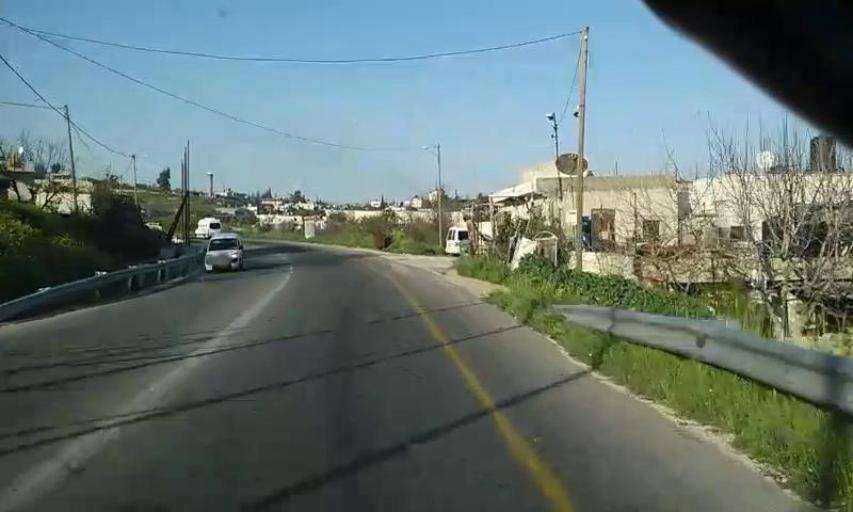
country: PS
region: West Bank
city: Bayt Ummar
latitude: 31.6153
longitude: 35.1146
